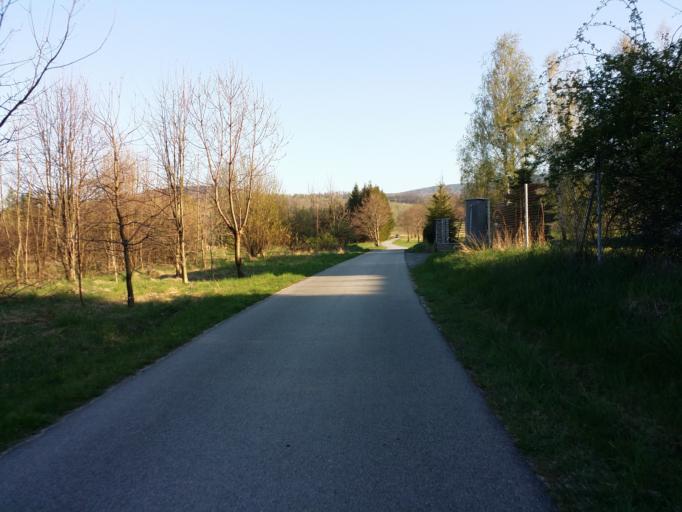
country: PL
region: Lower Silesian Voivodeship
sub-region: Powiat lwowecki
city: Mirsk
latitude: 50.9338
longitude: 15.4364
